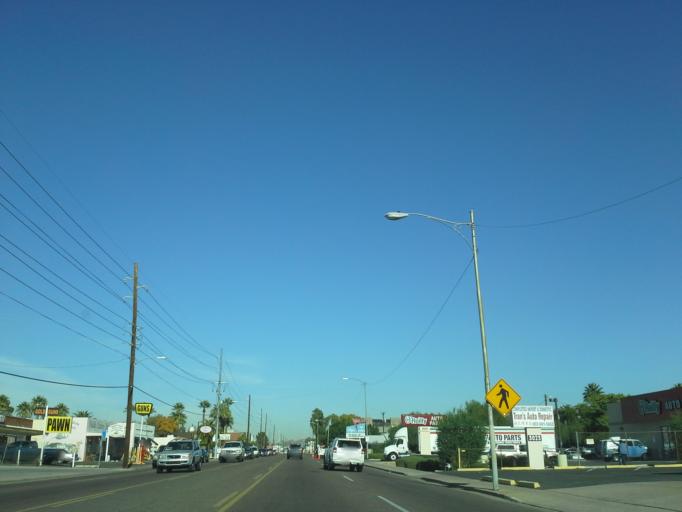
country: US
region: Arizona
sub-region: Maricopa County
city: Phoenix
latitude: 33.4827
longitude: -112.0476
